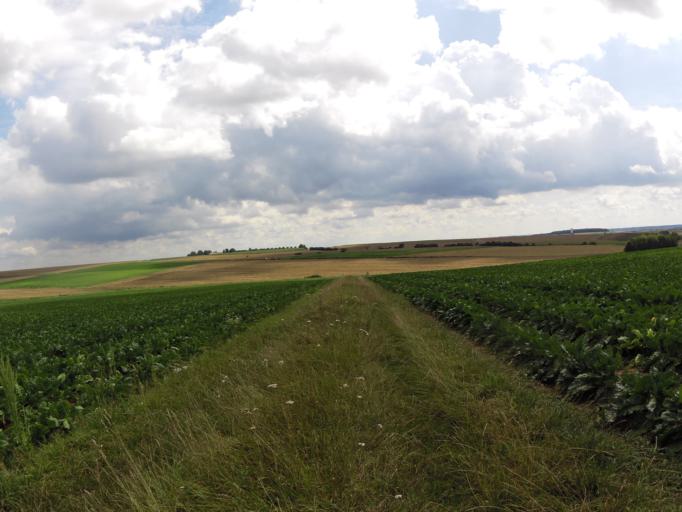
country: DE
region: Bavaria
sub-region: Regierungsbezirk Unterfranken
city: Geroldshausen
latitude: 49.6970
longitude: 9.8800
